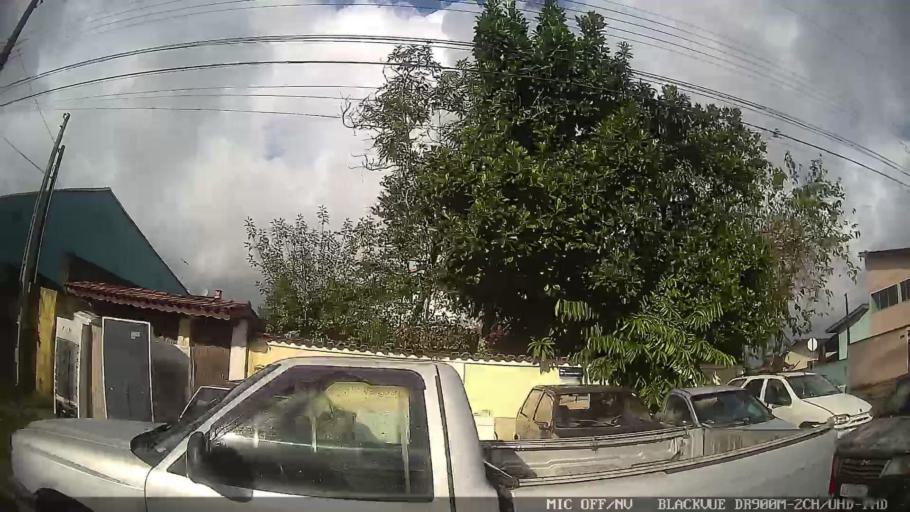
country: BR
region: Sao Paulo
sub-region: Itanhaem
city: Itanhaem
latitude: -24.2182
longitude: -46.8847
